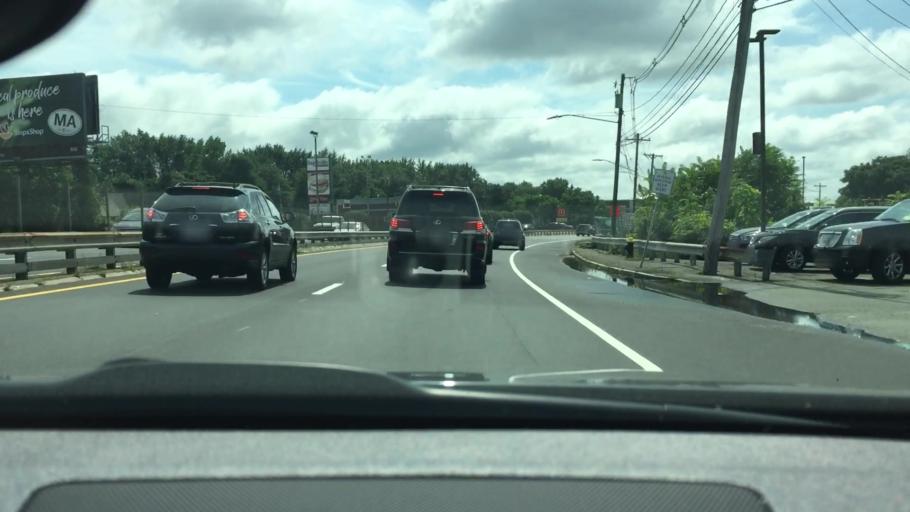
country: US
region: Massachusetts
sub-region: Norfolk County
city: Dedham
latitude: 42.2656
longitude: -71.1684
